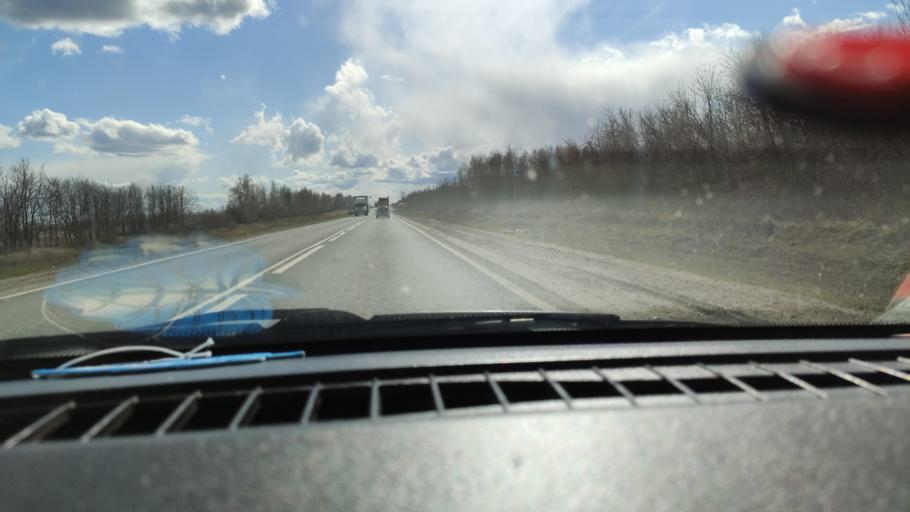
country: RU
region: Saratov
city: Dukhovnitskoye
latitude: 52.6824
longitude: 48.2344
